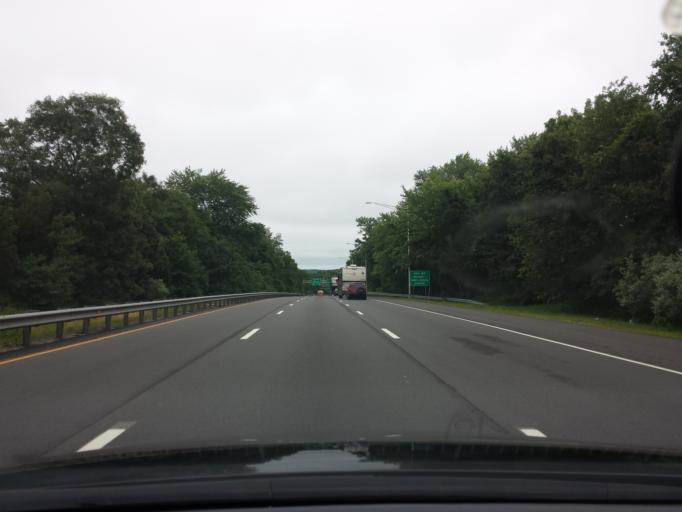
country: US
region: Connecticut
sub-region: New London County
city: Long Hill
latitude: 41.3636
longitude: -72.0645
